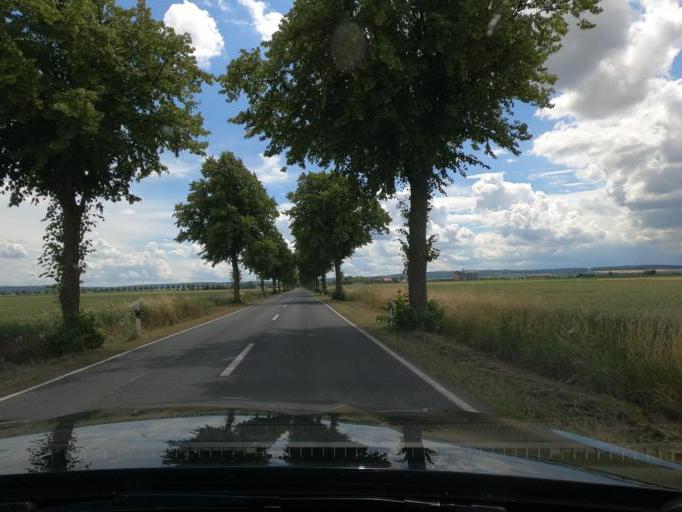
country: DE
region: Lower Saxony
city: Schellerten
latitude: 52.1862
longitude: 10.0397
